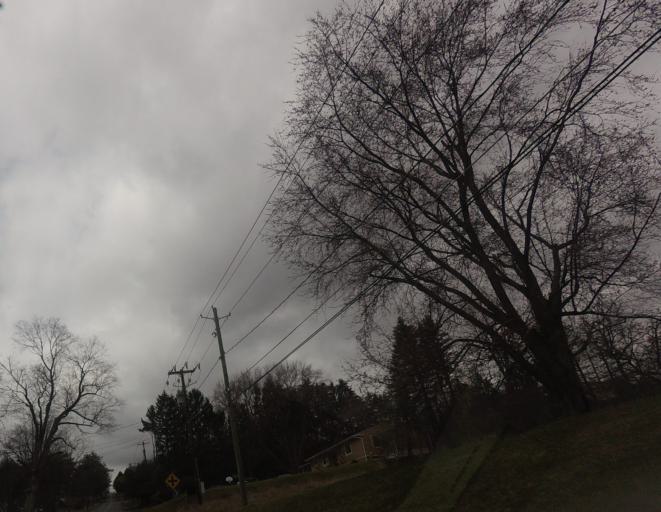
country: US
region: New York
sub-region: Tompkins County
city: Ithaca
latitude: 42.4361
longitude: -76.5318
